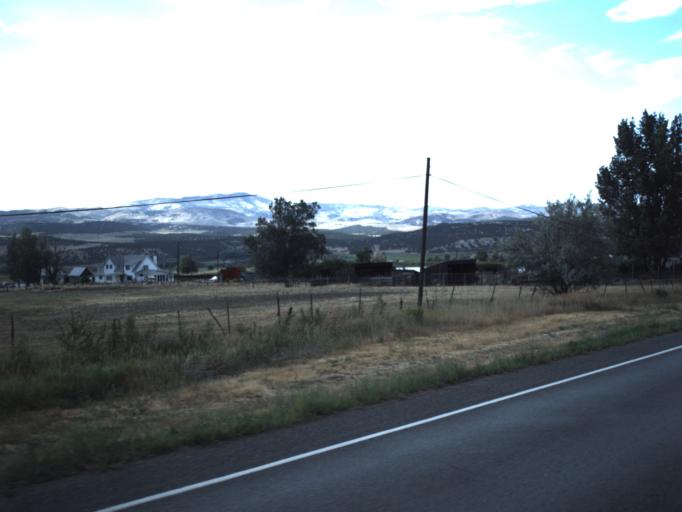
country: US
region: Utah
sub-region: Sanpete County
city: Mount Pleasant
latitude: 39.5604
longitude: -111.4555
